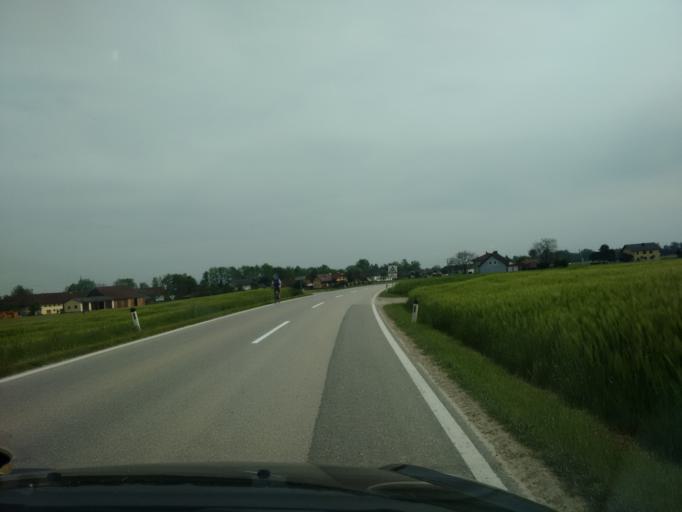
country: AT
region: Upper Austria
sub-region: Wels-Land
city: Marchtrenk
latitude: 48.1748
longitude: 14.1497
